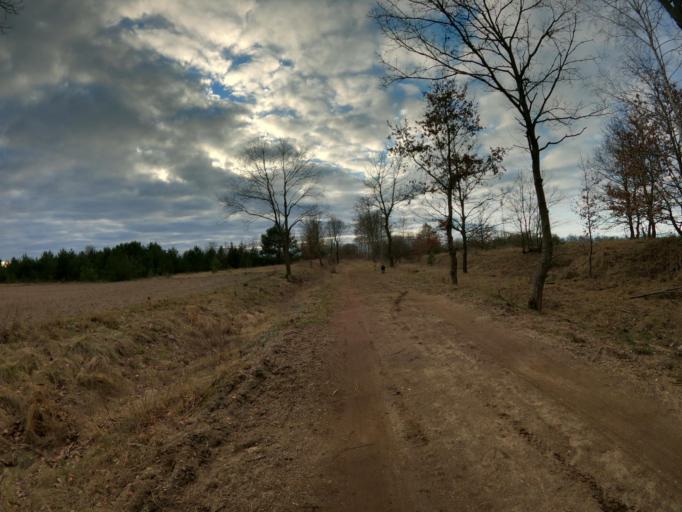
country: PL
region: West Pomeranian Voivodeship
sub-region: Powiat kamienski
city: Golczewo
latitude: 53.8286
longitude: 14.9889
